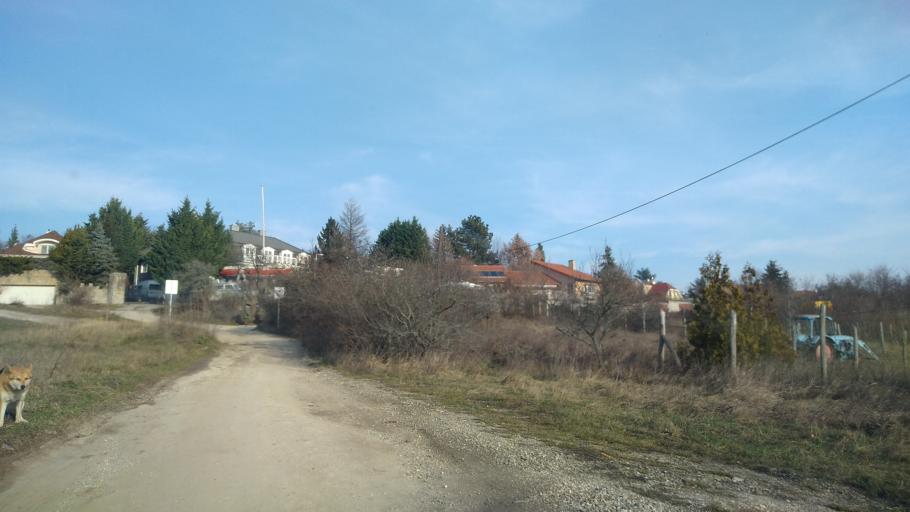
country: HU
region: Pest
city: Szentendre
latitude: 47.6904
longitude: 19.0587
